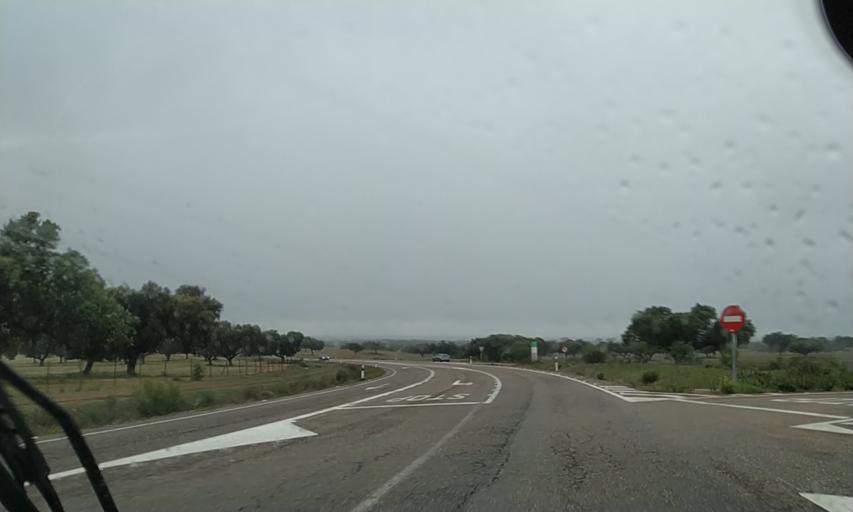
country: ES
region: Extremadura
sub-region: Provincia de Badajoz
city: La Roca de la Sierra
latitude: 39.1082
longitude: -6.7082
